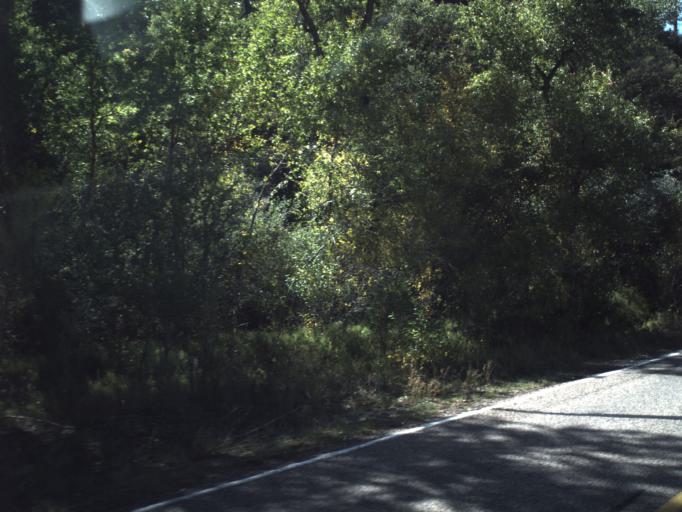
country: US
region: Utah
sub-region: Beaver County
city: Beaver
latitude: 38.2794
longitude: -112.5655
